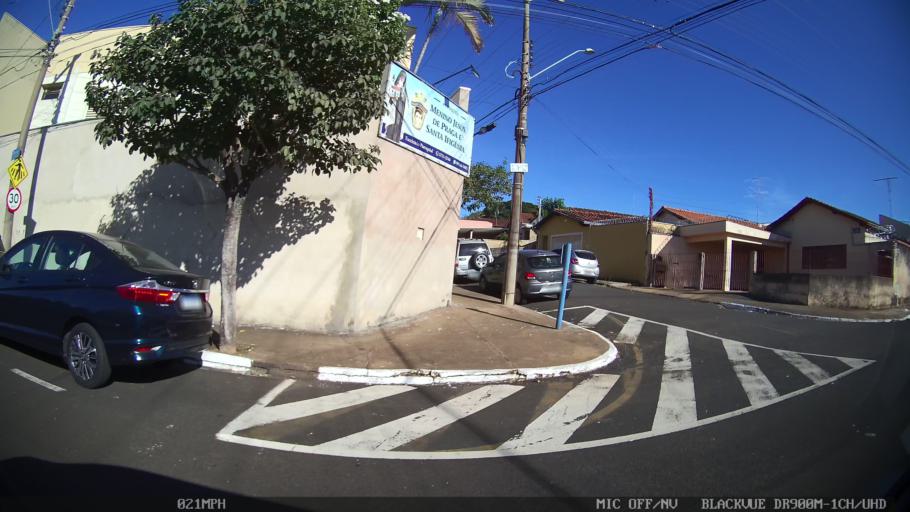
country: BR
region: Sao Paulo
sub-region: Franca
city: Franca
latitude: -20.5449
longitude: -47.4115
